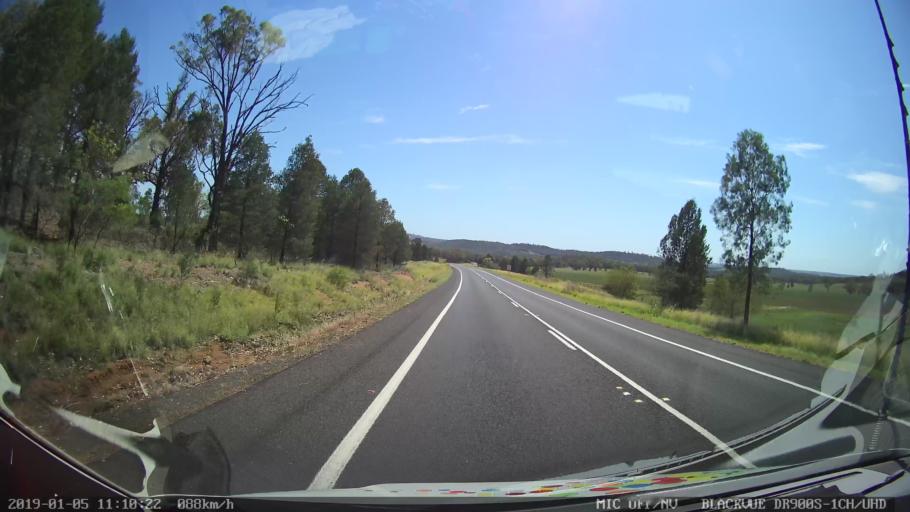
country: AU
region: New South Wales
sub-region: Warrumbungle Shire
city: Coonabarabran
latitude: -31.4072
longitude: 149.2437
